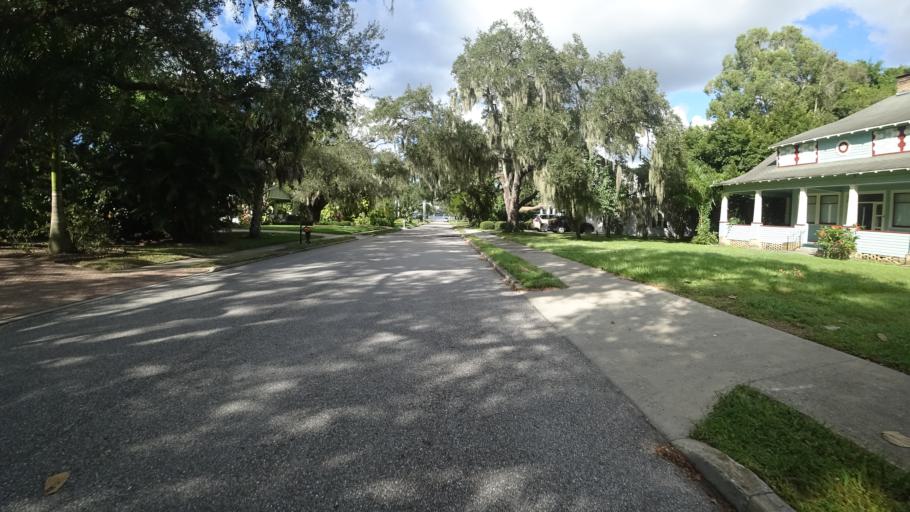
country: US
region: Florida
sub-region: Manatee County
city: Bradenton
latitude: 27.4980
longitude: -82.5861
